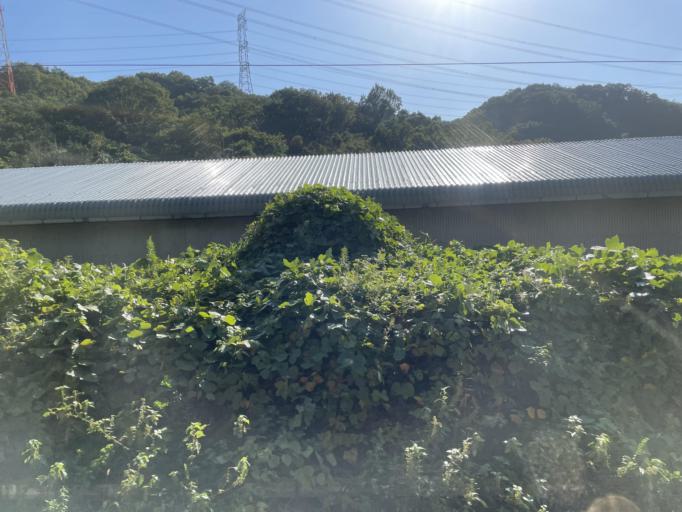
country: JP
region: Osaka
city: Kashihara
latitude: 34.5347
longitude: 135.6578
